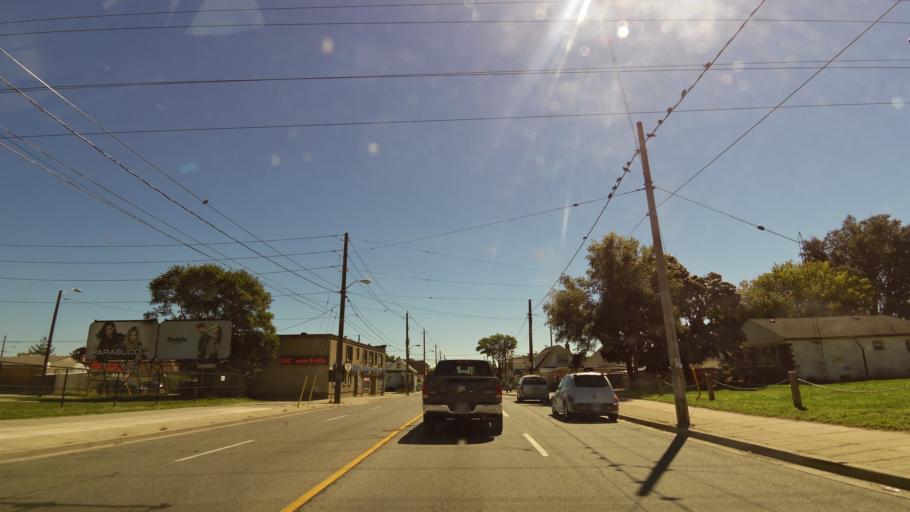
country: CA
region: Ontario
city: Etobicoke
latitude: 43.6710
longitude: -79.4935
